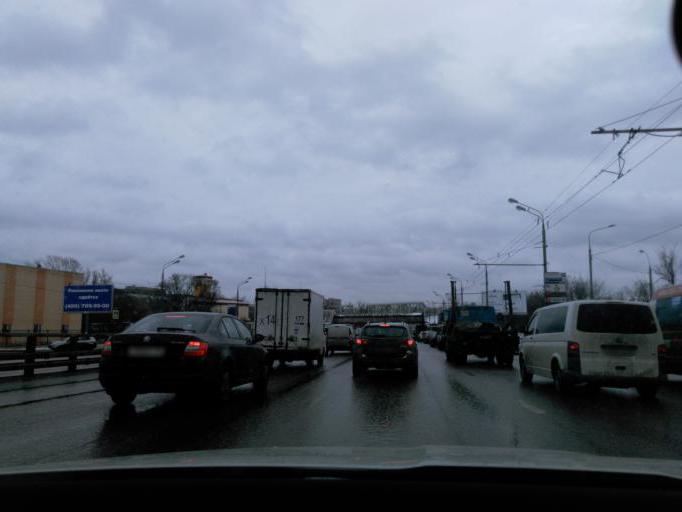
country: RU
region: Moscow
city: Likhobory
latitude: 55.8534
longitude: 37.5636
